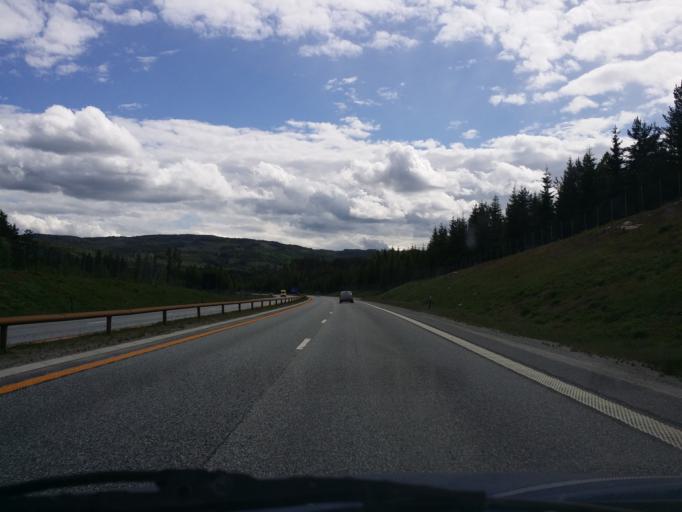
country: NO
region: Hedmark
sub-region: Stange
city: Stange
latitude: 60.6210
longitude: 11.2994
